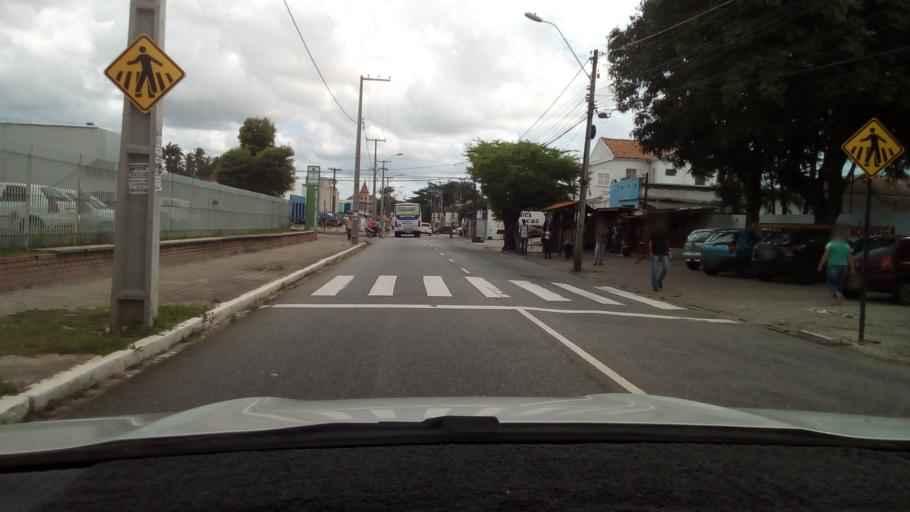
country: BR
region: Paraiba
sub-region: Joao Pessoa
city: Joao Pessoa
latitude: -7.1332
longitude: -34.8817
